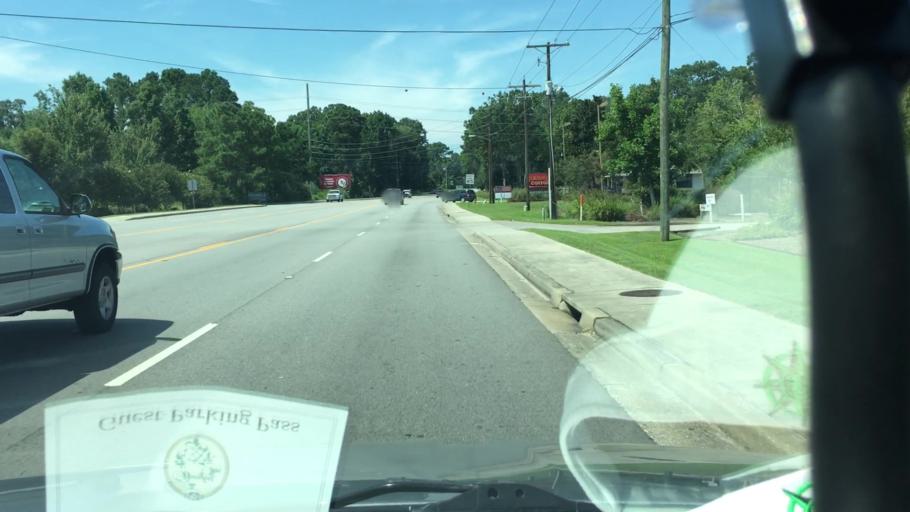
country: US
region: South Carolina
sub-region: Beaufort County
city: Burton
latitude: 32.4340
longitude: -80.7122
